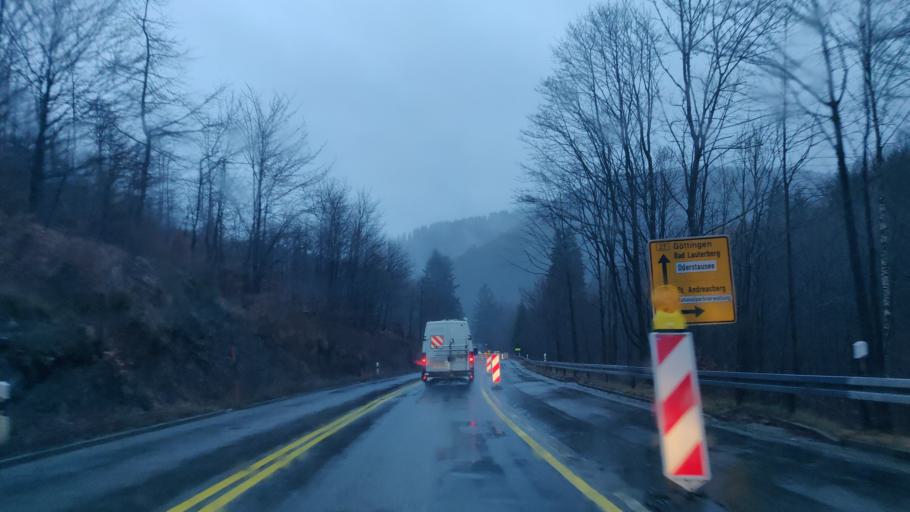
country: DE
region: Lower Saxony
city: Braunlage
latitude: 51.6983
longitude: 10.5690
